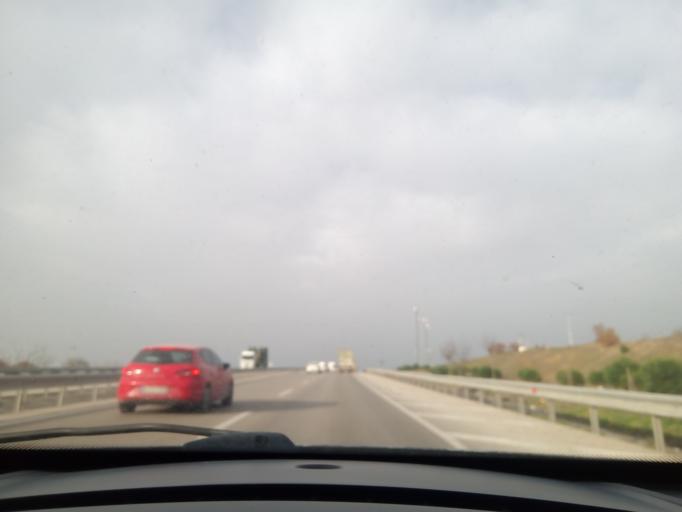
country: TR
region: Bursa
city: Mahmudiye
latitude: 40.2127
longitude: 28.6867
